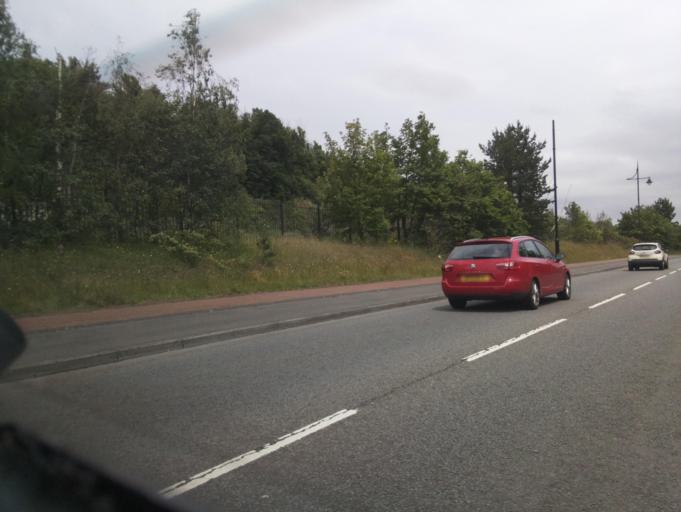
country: GB
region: Wales
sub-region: Vale of Glamorgan
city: Barry
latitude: 51.4072
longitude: -3.2554
